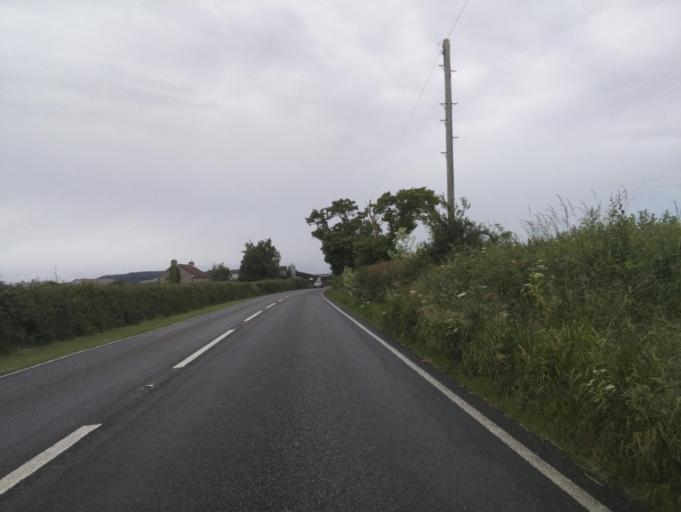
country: GB
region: England
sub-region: Devon
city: Colyton
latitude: 50.7367
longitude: -3.0426
